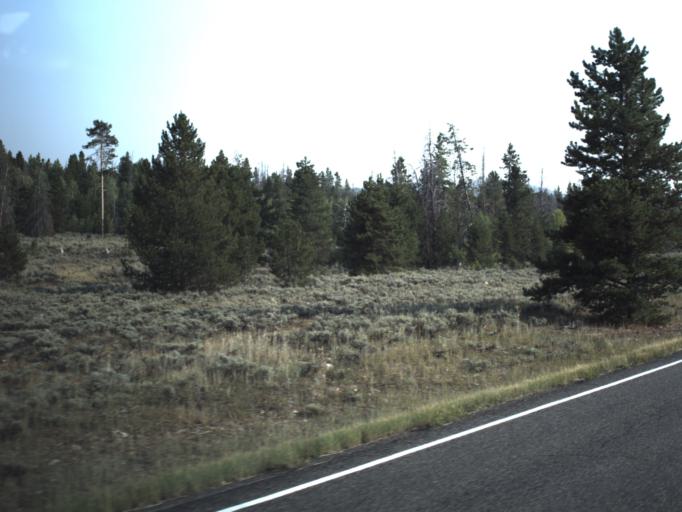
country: US
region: Wyoming
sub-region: Uinta County
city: Evanston
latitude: 40.8976
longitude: -110.8294
